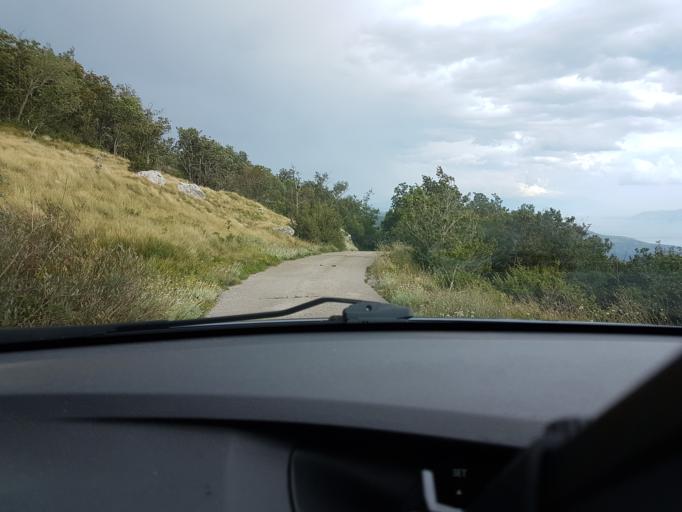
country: HR
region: Primorsko-Goranska
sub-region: Grad Crikvenica
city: Crikvenica
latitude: 45.2392
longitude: 14.6932
